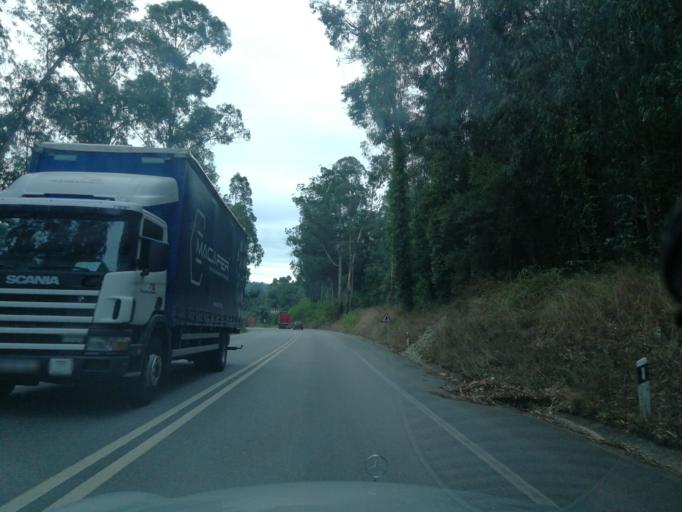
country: PT
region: Aveiro
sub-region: Agueda
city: Valongo
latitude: 40.6520
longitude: -8.4666
